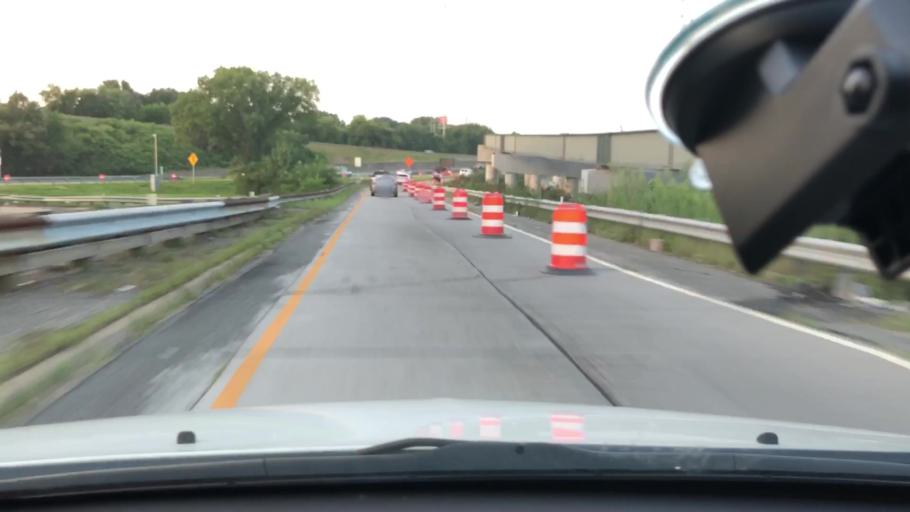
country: US
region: Virginia
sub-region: City of Chesapeake
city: Chesapeake
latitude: 36.8434
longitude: -76.1953
